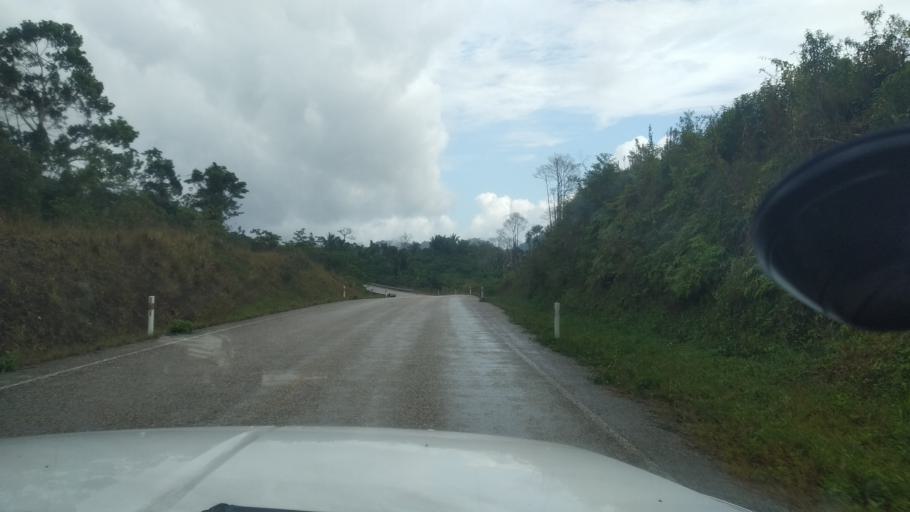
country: GT
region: Peten
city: San Luis
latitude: 16.1960
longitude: -89.1647
